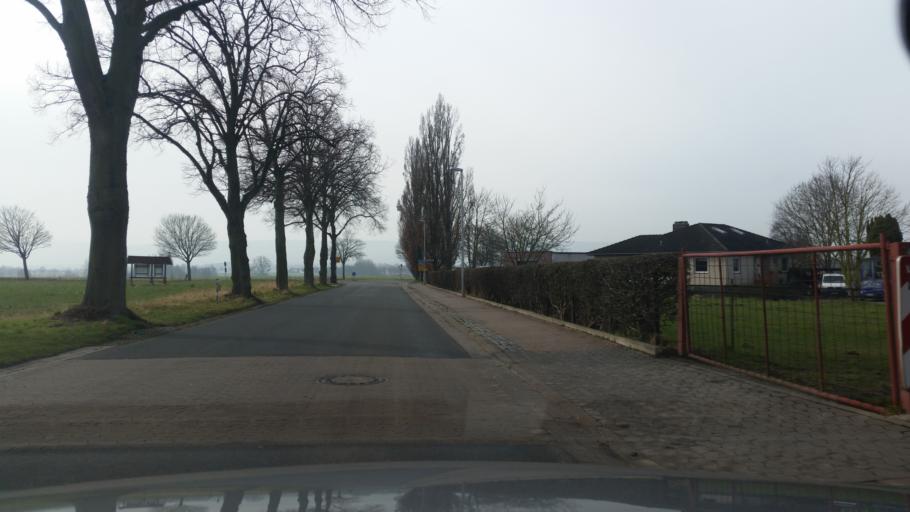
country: DE
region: Lower Saxony
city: Grossgoltern
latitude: 52.3420
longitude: 9.5175
